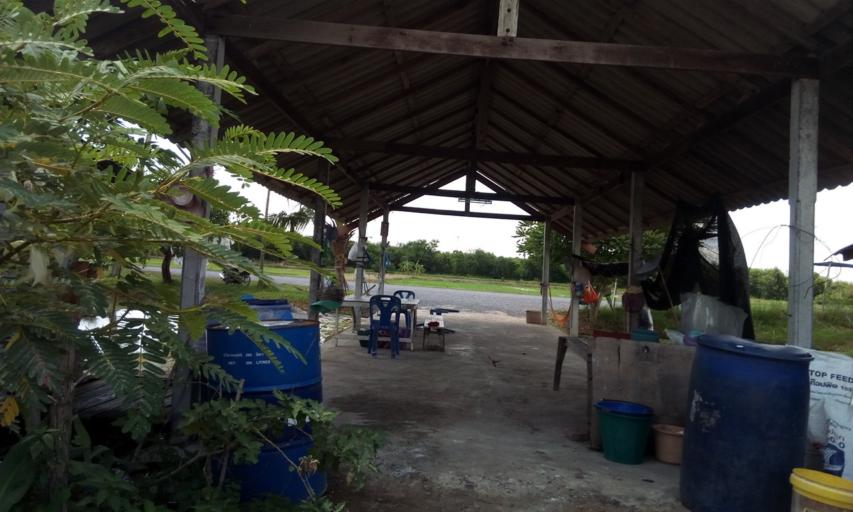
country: TH
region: Pathum Thani
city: Ban Lam Luk Ka
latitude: 13.9894
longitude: 100.8393
